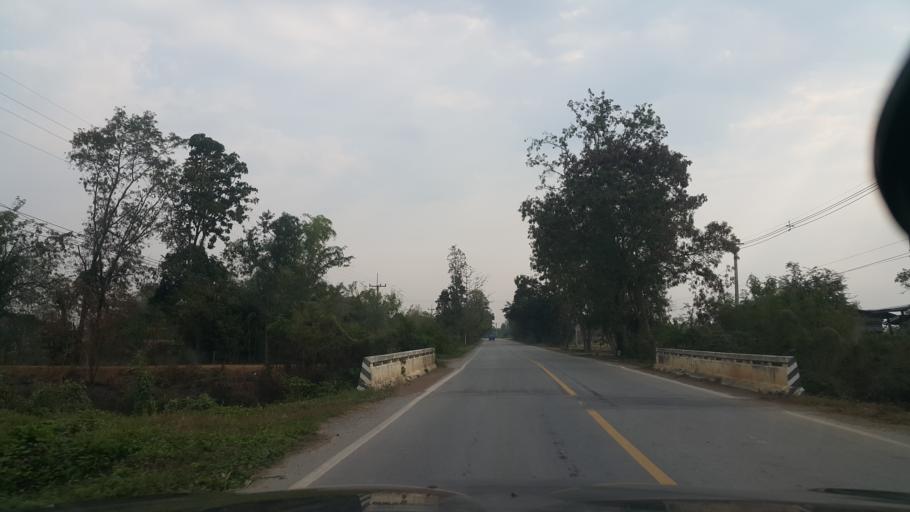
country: TH
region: Sukhothai
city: Si Samrong
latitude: 17.1714
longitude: 99.7262
